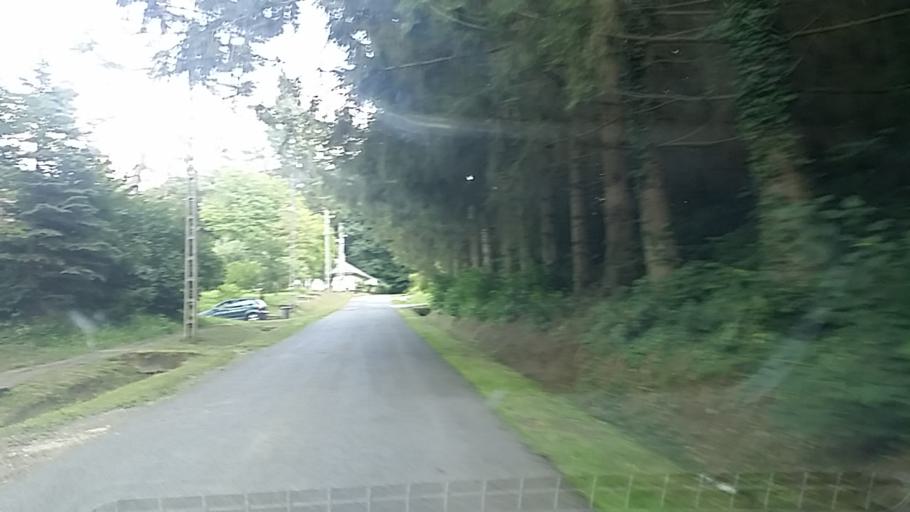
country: HU
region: Zala
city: Becsehely
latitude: 46.5205
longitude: 16.7304
